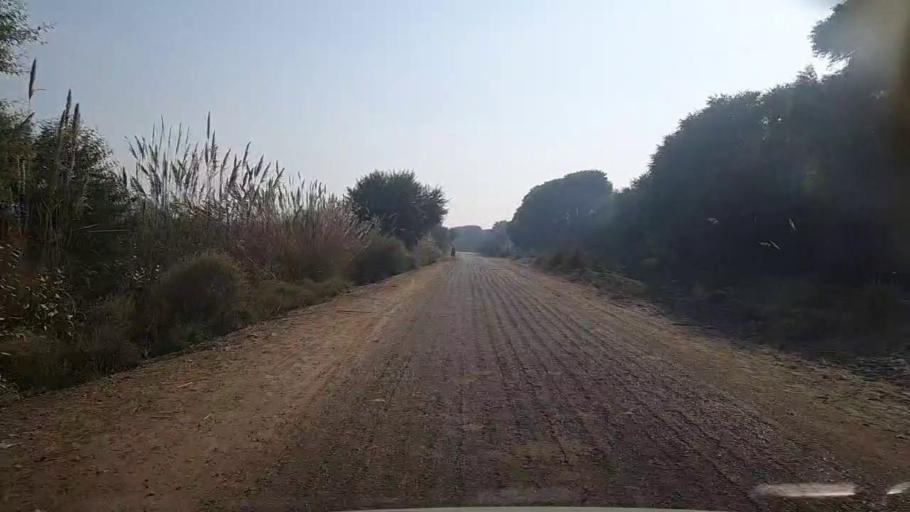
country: PK
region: Sindh
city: Kandiari
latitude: 26.8400
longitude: 68.4892
